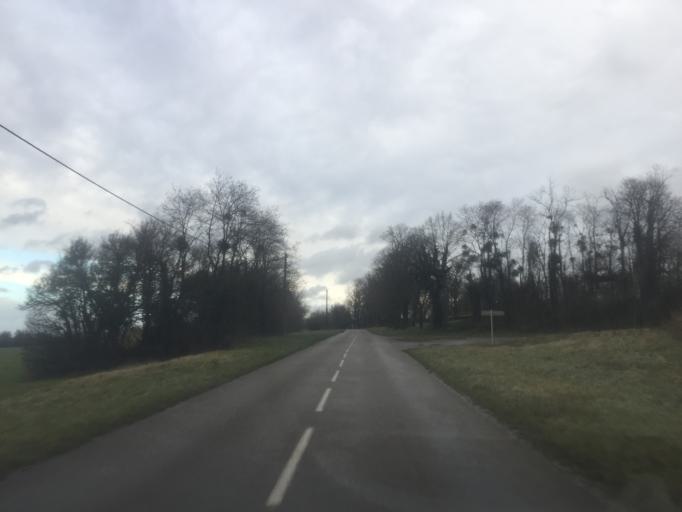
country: FR
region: Franche-Comte
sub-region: Departement de la Haute-Saone
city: Pesmes
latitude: 47.2188
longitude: 5.5293
